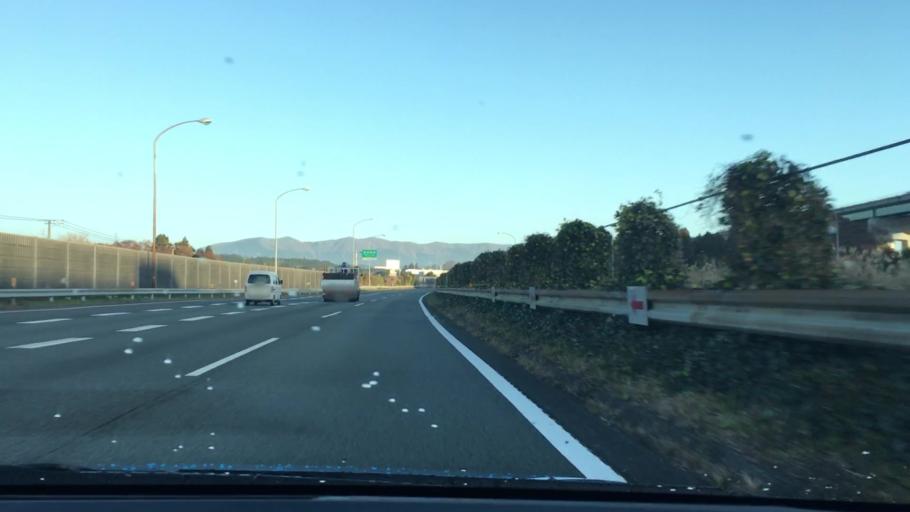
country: JP
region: Shizuoka
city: Gotemba
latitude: 35.2548
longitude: 138.9095
